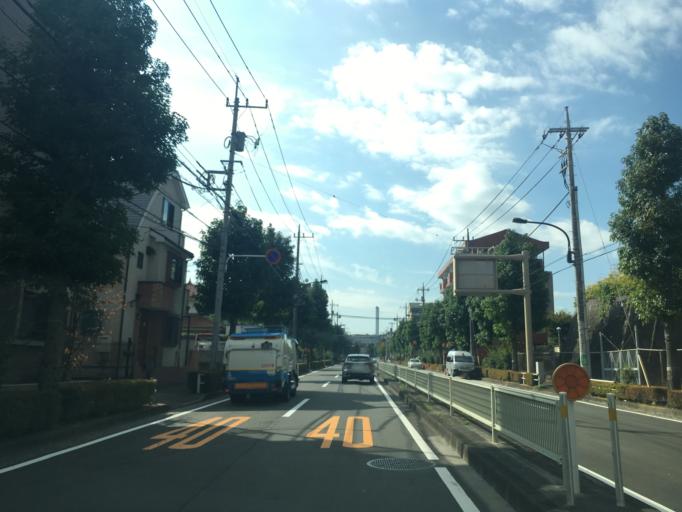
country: JP
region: Tokyo
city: Hino
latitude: 35.6214
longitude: 139.4160
